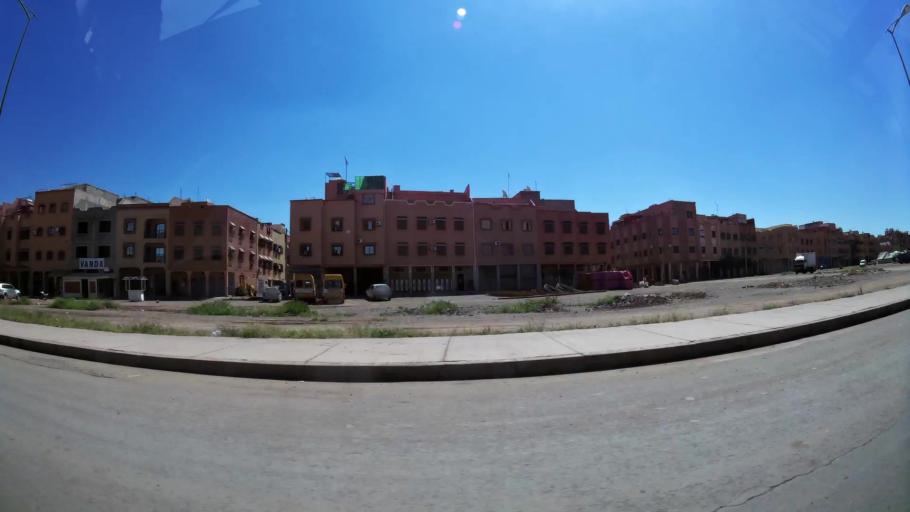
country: MA
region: Marrakech-Tensift-Al Haouz
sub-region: Marrakech
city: Marrakesh
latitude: 31.6321
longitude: -8.0712
